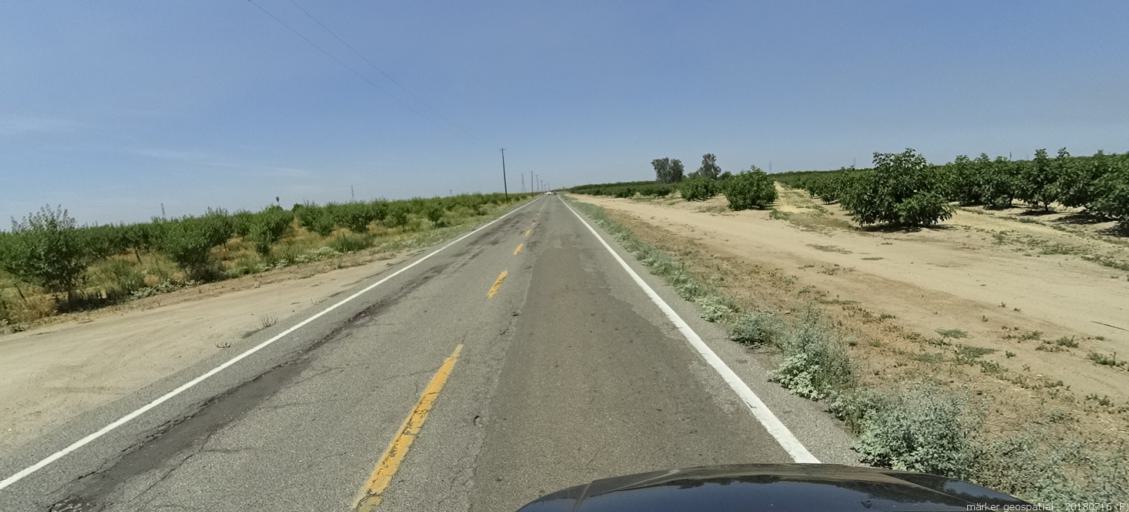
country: US
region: California
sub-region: Madera County
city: Madera Acres
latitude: 37.0491
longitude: -120.1062
